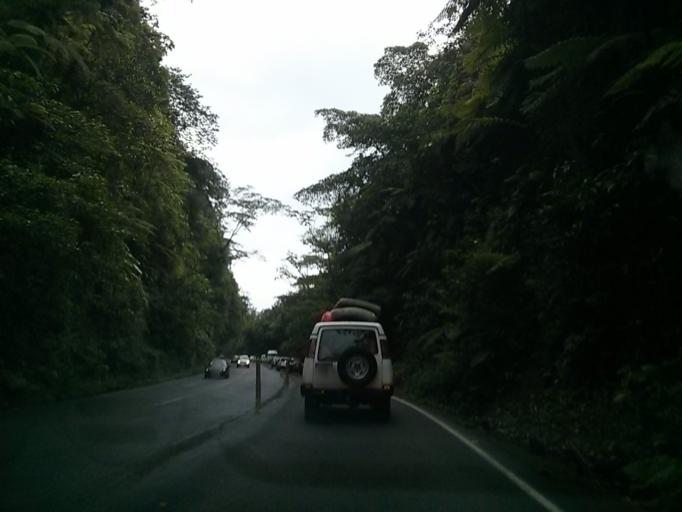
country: CR
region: San Jose
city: Dulce Nombre de Jesus
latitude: 10.1470
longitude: -83.9743
